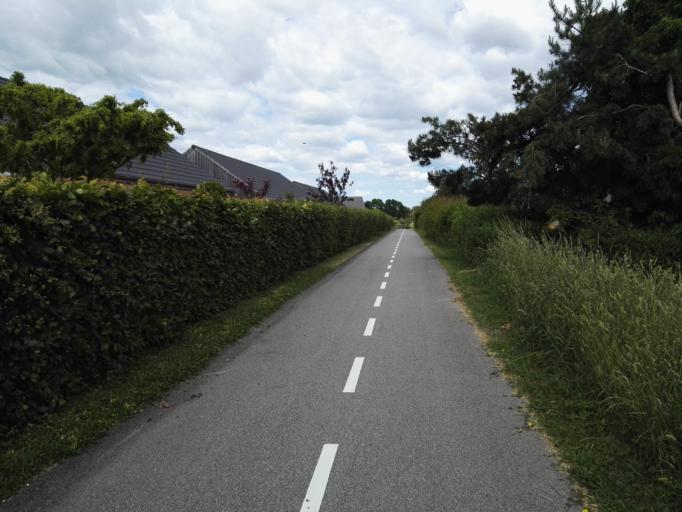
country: DK
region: Capital Region
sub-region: Egedal Kommune
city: Stenlose
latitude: 55.7649
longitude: 12.1783
